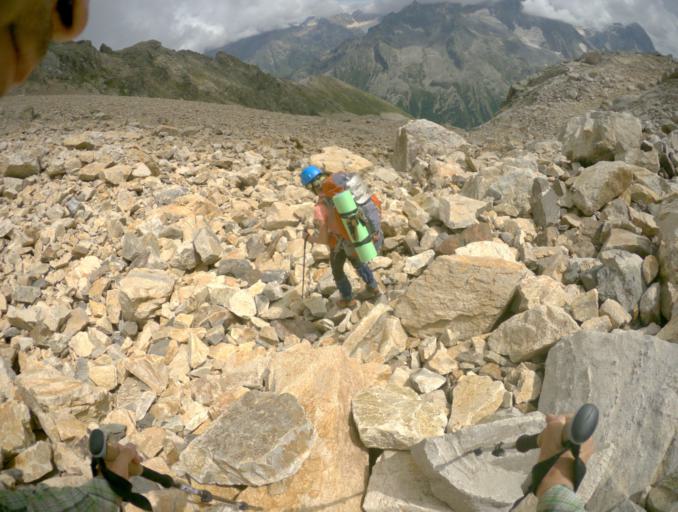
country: RU
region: Karachayevo-Cherkesiya
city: Uchkulan
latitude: 43.2769
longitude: 42.1190
